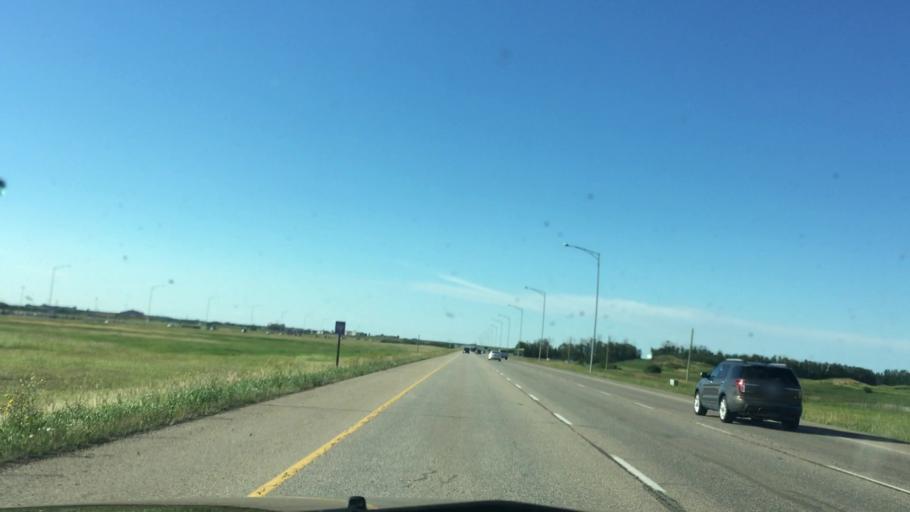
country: CA
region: Alberta
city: Leduc
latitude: 53.3290
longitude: -113.5499
